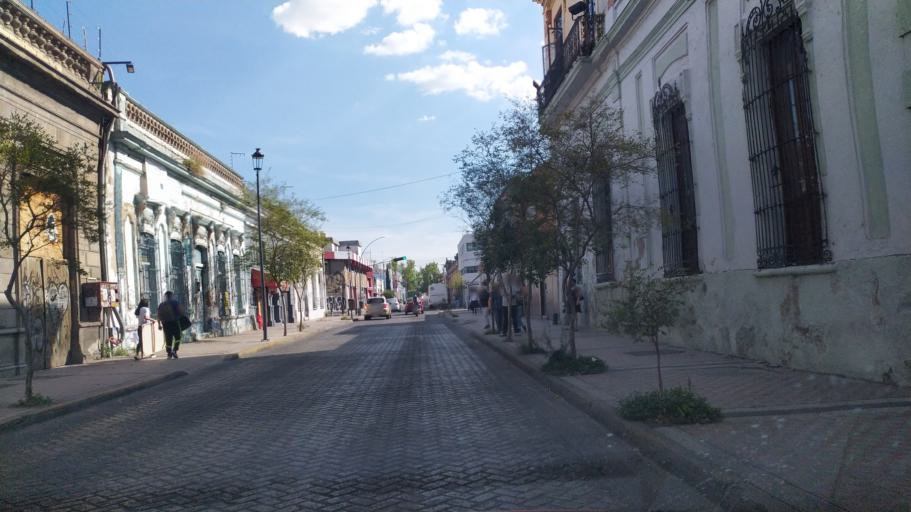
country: MX
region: Jalisco
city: Guadalajara
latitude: 20.6734
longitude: -103.3524
